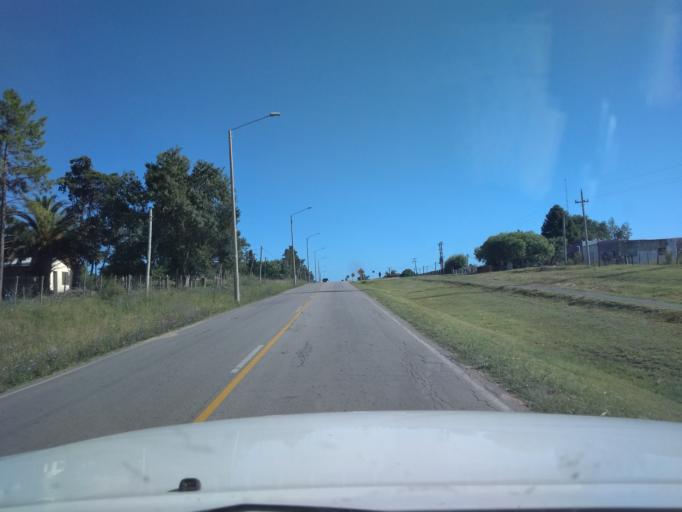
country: UY
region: Canelones
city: San Ramon
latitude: -34.3061
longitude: -55.9583
